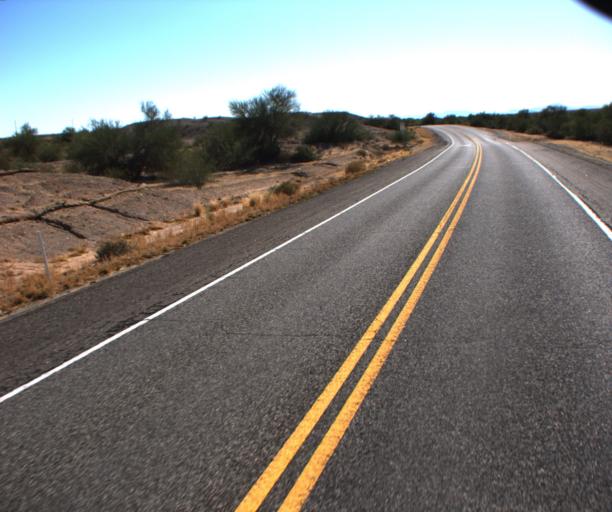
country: US
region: Arizona
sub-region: La Paz County
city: Parker
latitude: 33.9930
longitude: -114.2093
